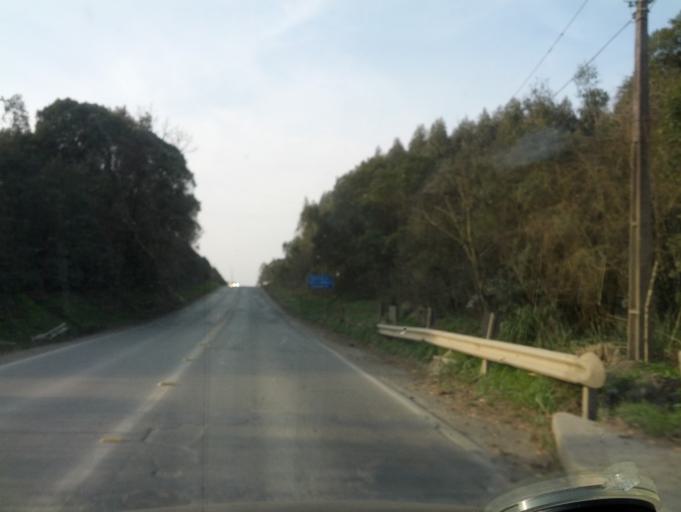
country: BR
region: Santa Catarina
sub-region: Otacilio Costa
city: Otacilio Costa
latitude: -27.5151
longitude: -50.1324
